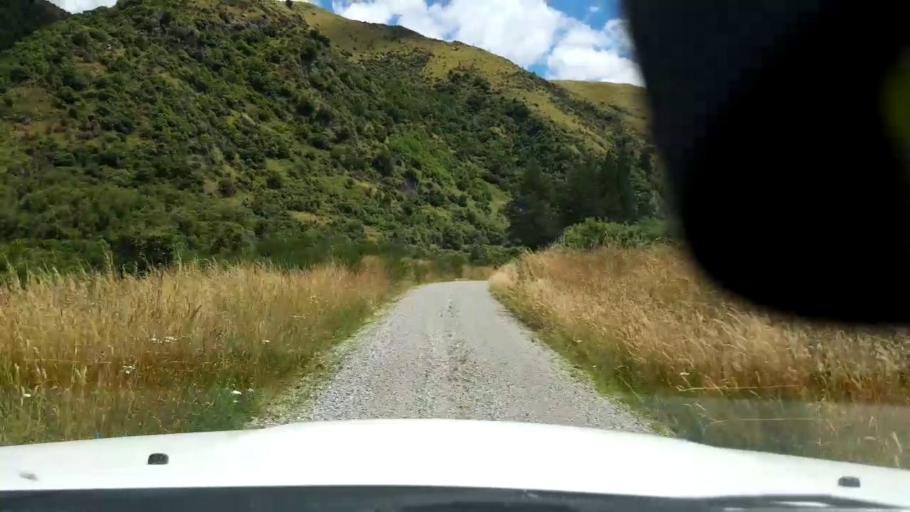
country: NZ
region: Canterbury
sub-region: Timaru District
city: Pleasant Point
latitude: -43.9328
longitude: 171.1961
